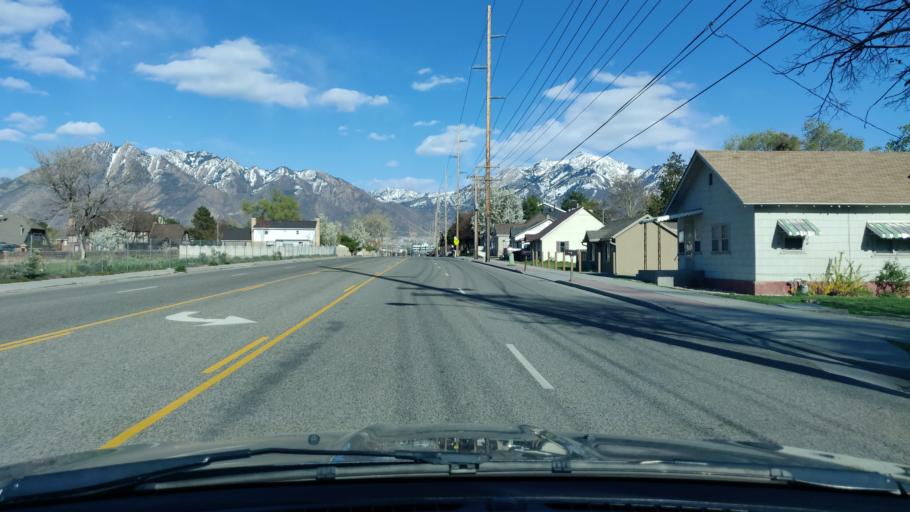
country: US
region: Utah
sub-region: Salt Lake County
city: Midvale
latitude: 40.6322
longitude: -111.8756
